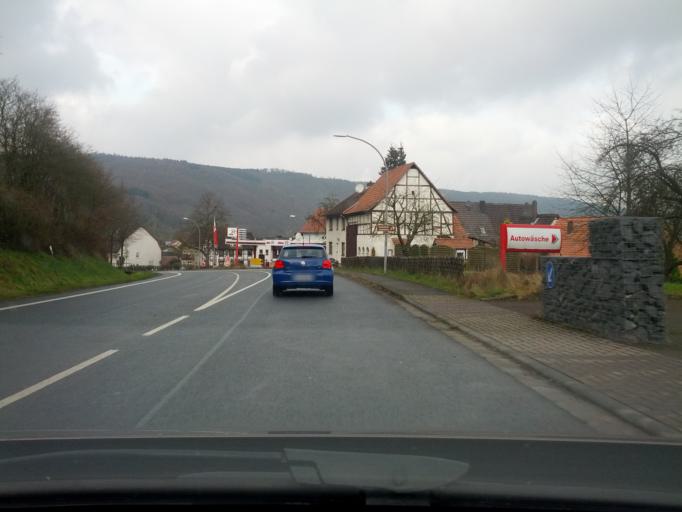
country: DE
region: Lower Saxony
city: Bodenfelde
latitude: 51.5963
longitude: 9.5495
